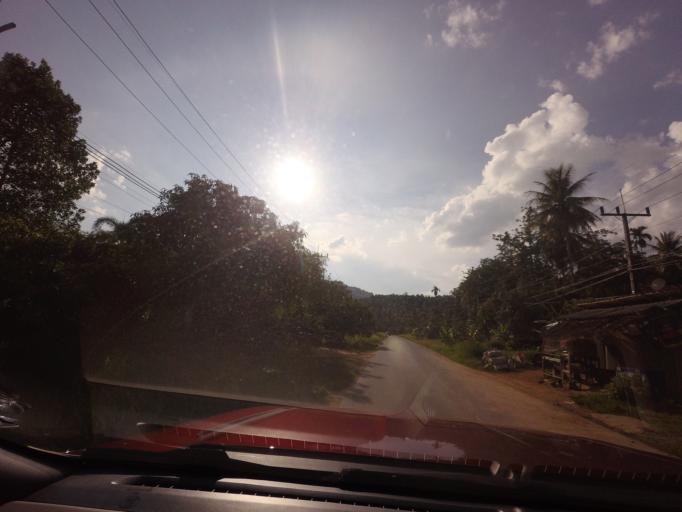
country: TH
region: Yala
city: Than To
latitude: 6.1970
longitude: 101.2416
